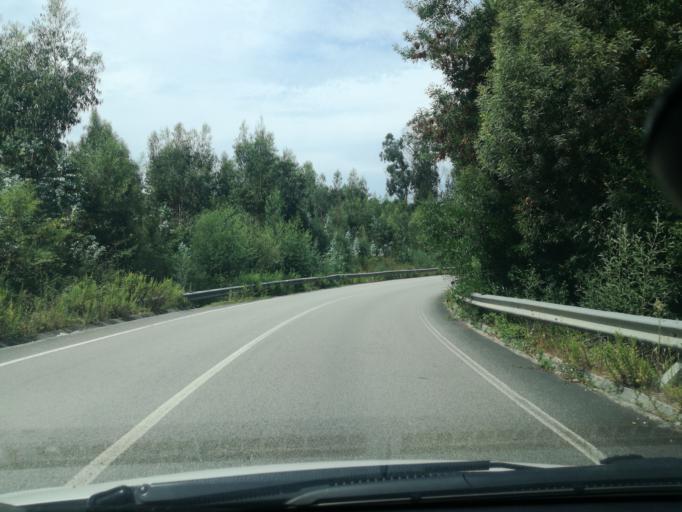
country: PT
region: Aveiro
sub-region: Santa Maria da Feira
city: Nogueira da Regedoura
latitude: 41.0134
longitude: -8.5845
